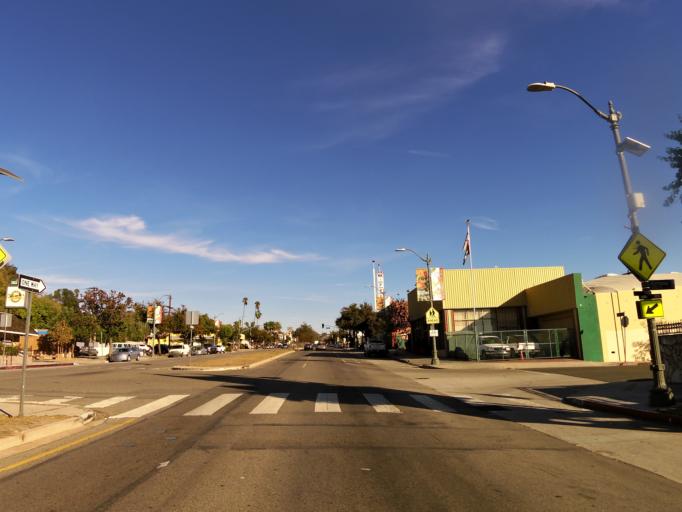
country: US
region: California
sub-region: Los Angeles County
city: Glendale
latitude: 34.1393
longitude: -118.2077
